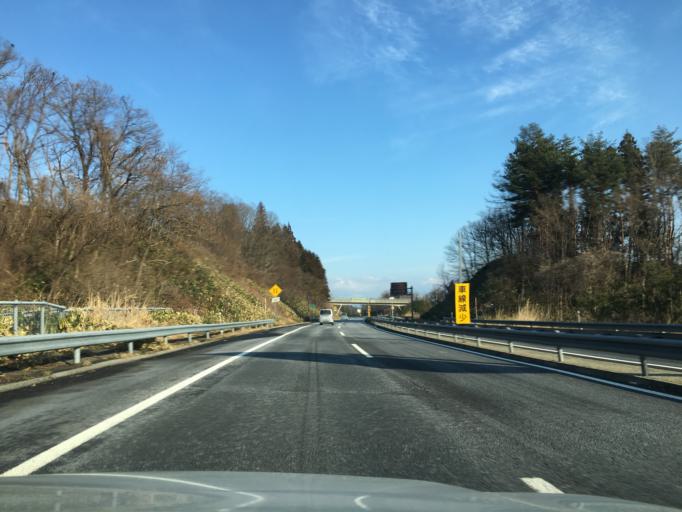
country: JP
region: Yamagata
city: Sagae
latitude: 38.4230
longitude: 140.1698
